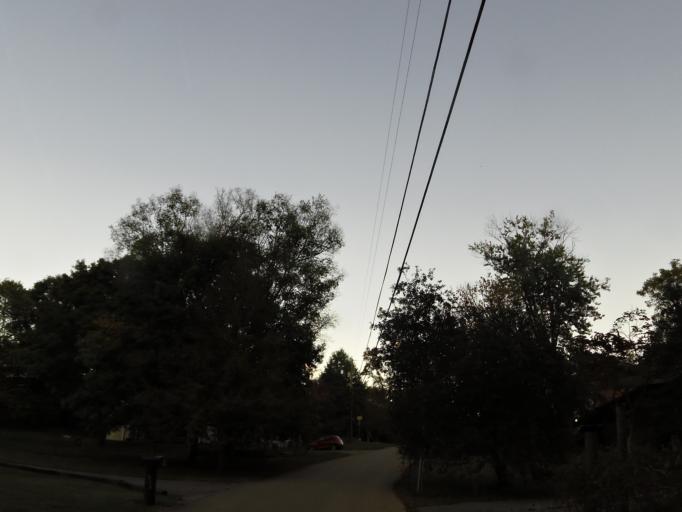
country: US
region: Tennessee
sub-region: Blount County
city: Maryville
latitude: 35.7724
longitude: -83.9498
